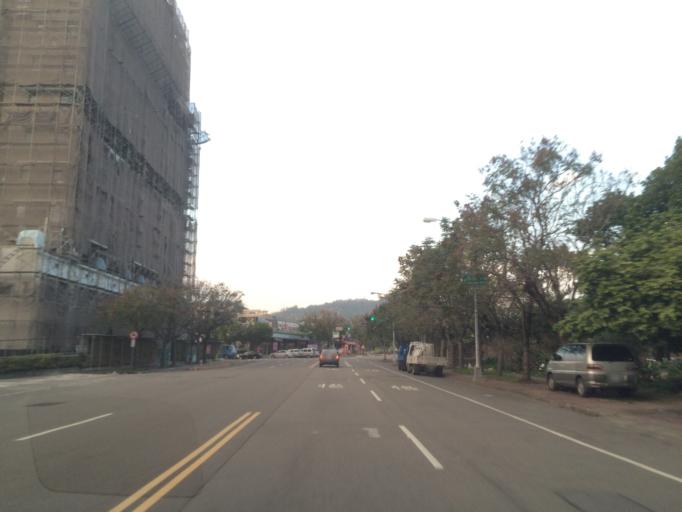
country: TW
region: Taiwan
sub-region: Taichung City
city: Taichung
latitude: 24.1693
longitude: 120.7334
